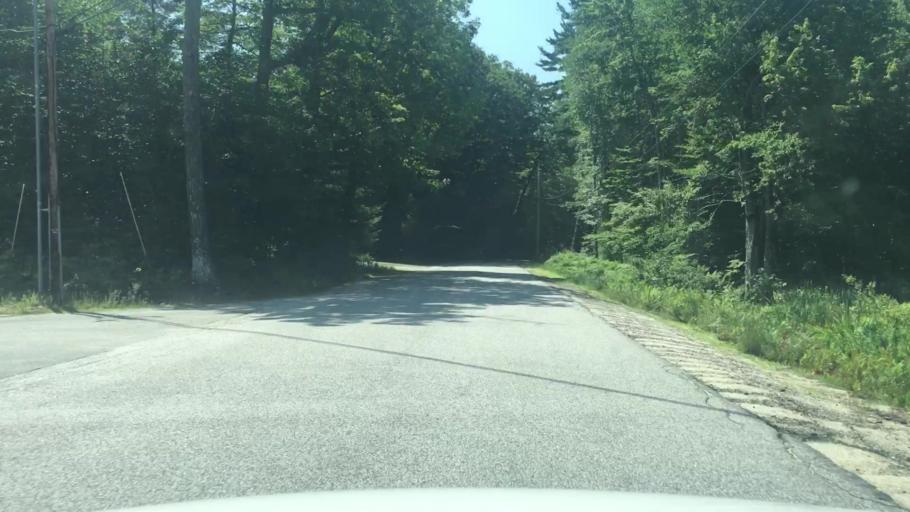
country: US
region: Maine
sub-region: Cumberland County
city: Cumberland Center
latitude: 43.8441
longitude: -70.3100
